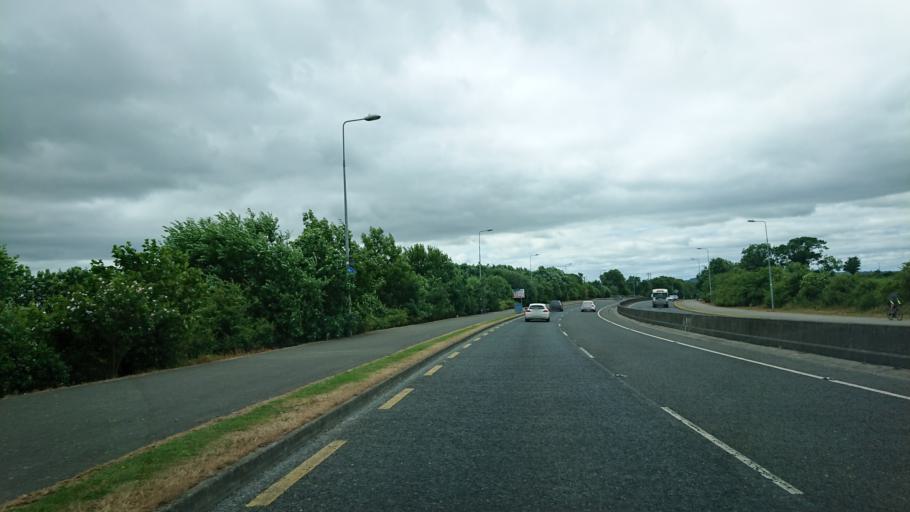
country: IE
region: Munster
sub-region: Waterford
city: Waterford
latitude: 52.2386
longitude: -7.0926
